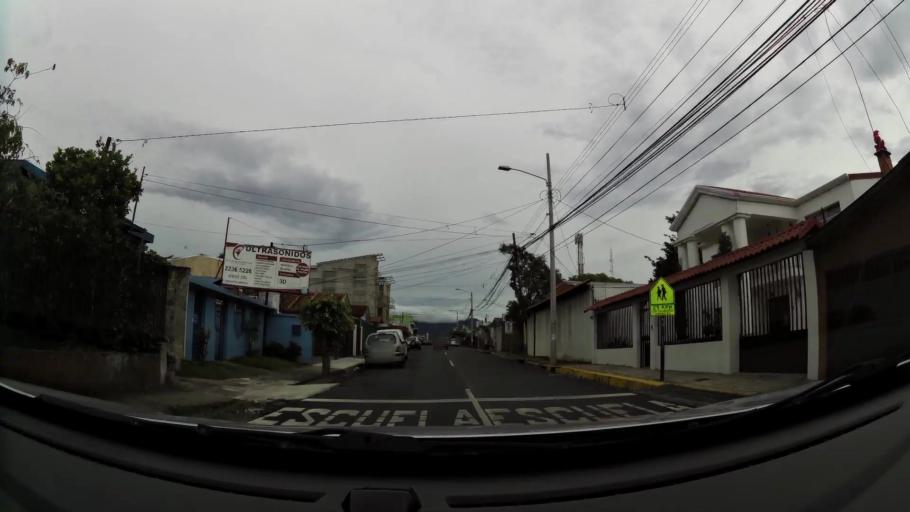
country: CR
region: San Jose
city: San Vicente
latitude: 9.9590
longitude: -84.0473
